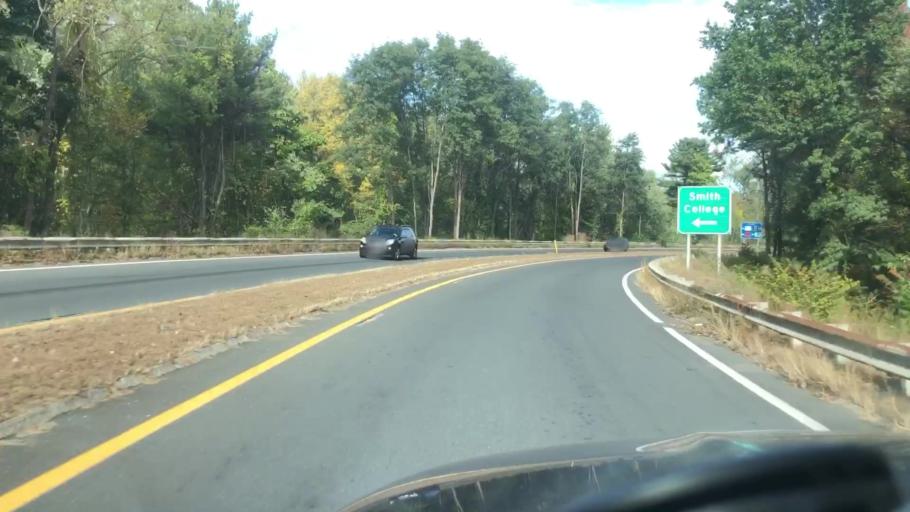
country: US
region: Massachusetts
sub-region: Hampshire County
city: Northampton
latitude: 42.3079
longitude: -72.6260
